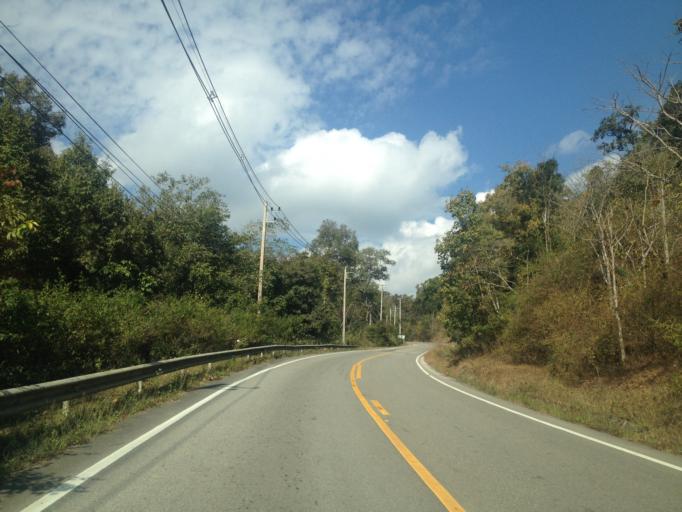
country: TH
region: Mae Hong Son
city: Ban Huai I Huak
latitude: 18.1384
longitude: 98.1739
